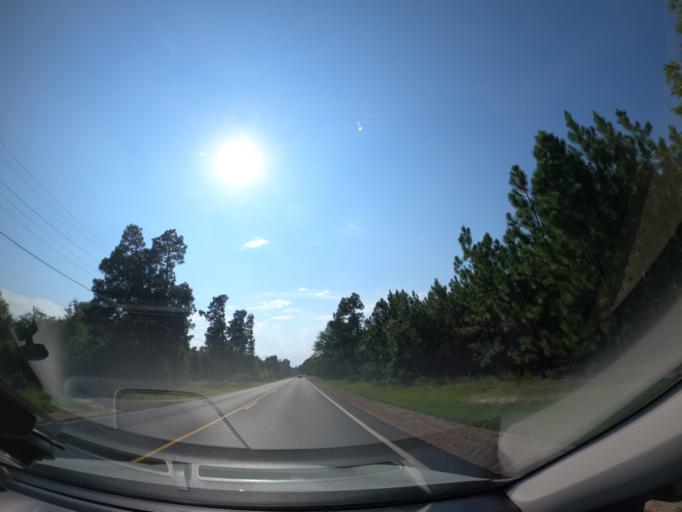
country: US
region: South Carolina
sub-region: Aiken County
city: New Ellenton
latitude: 33.3934
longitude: -81.7316
